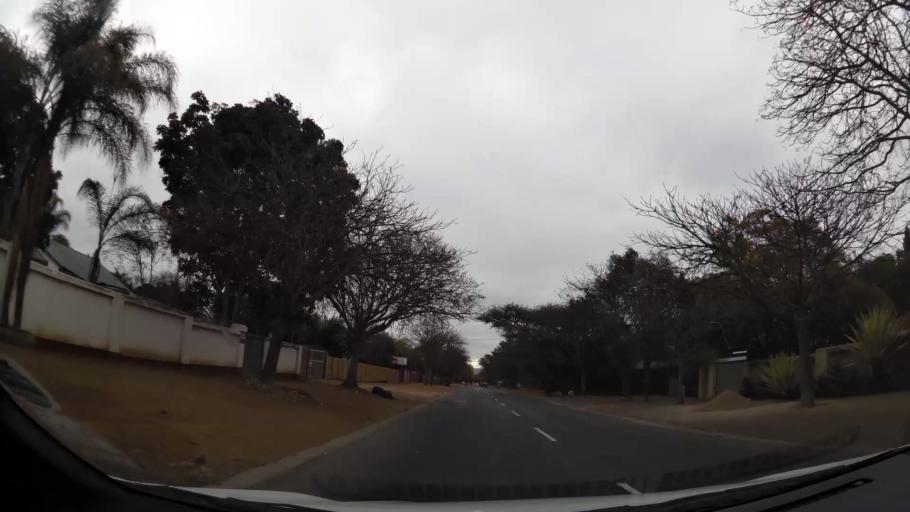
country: ZA
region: Limpopo
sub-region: Capricorn District Municipality
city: Polokwane
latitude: -23.9011
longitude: 29.4700
